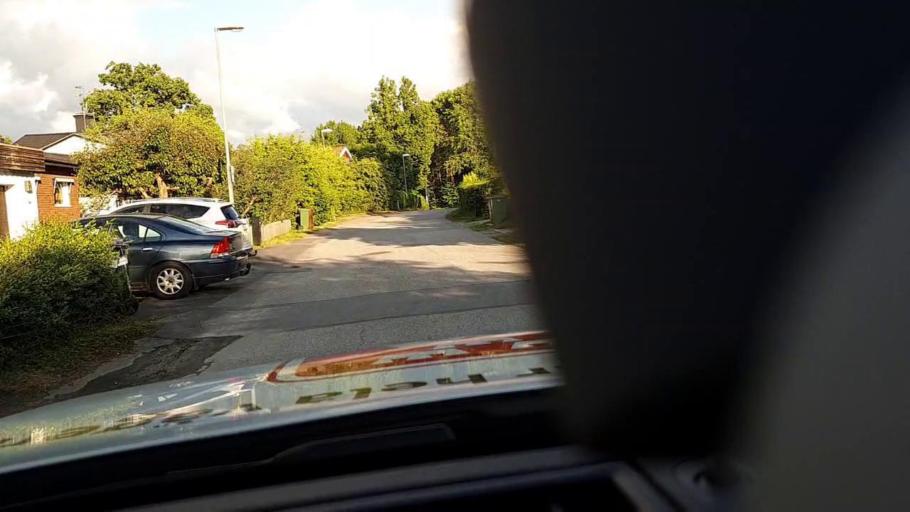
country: SE
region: Stockholm
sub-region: Huddinge Kommun
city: Huddinge
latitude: 59.2454
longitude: 17.9728
